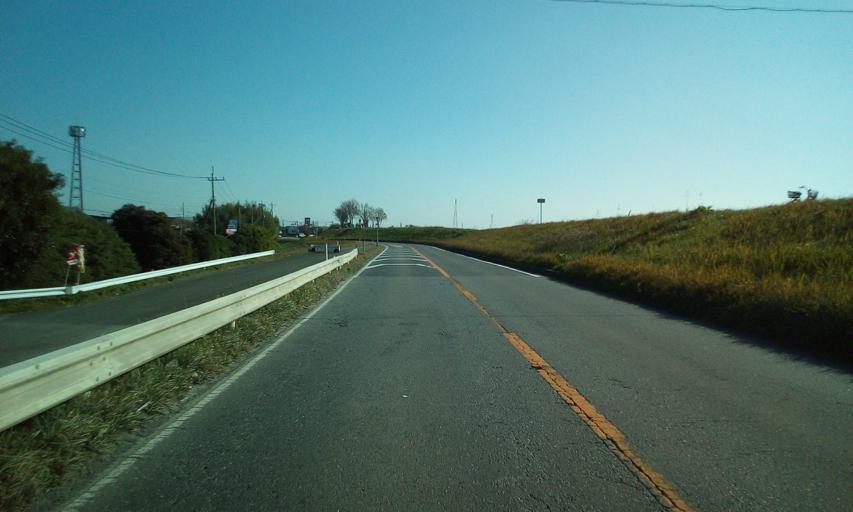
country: JP
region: Ibaraki
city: Sakai
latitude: 36.1091
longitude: 139.7847
